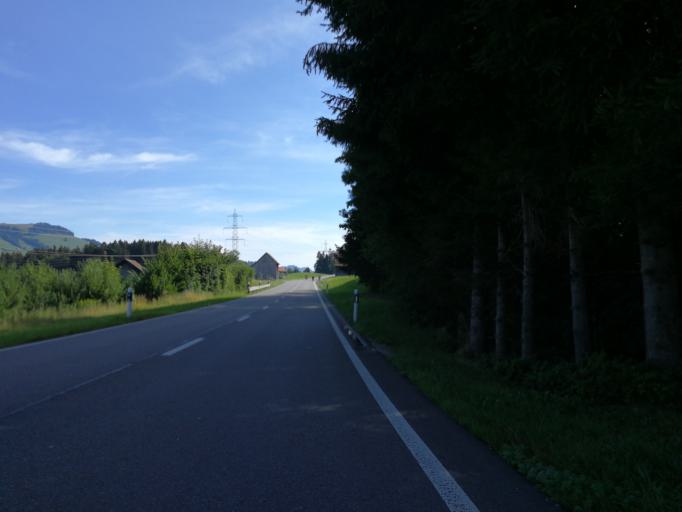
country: CH
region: Saint Gallen
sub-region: Wahlkreis See-Gaster
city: Gommiswald
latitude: 47.2519
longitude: 9.0338
